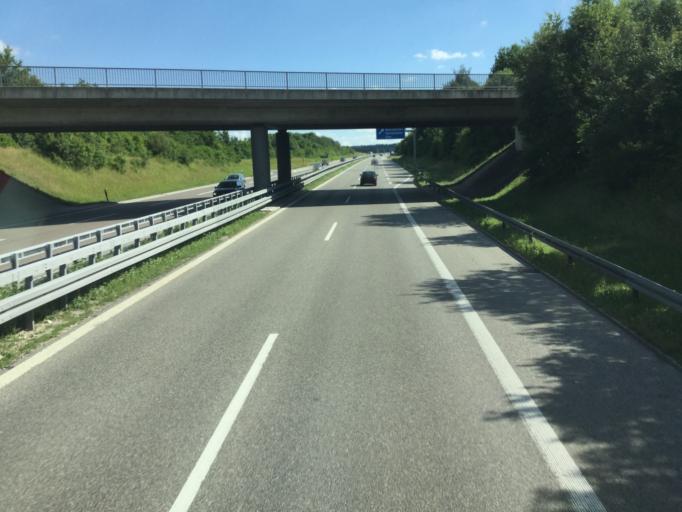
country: DE
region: Baden-Wuerttemberg
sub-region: Tuebingen Region
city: Leutkirch im Allgau
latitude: 47.8179
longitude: 9.9910
